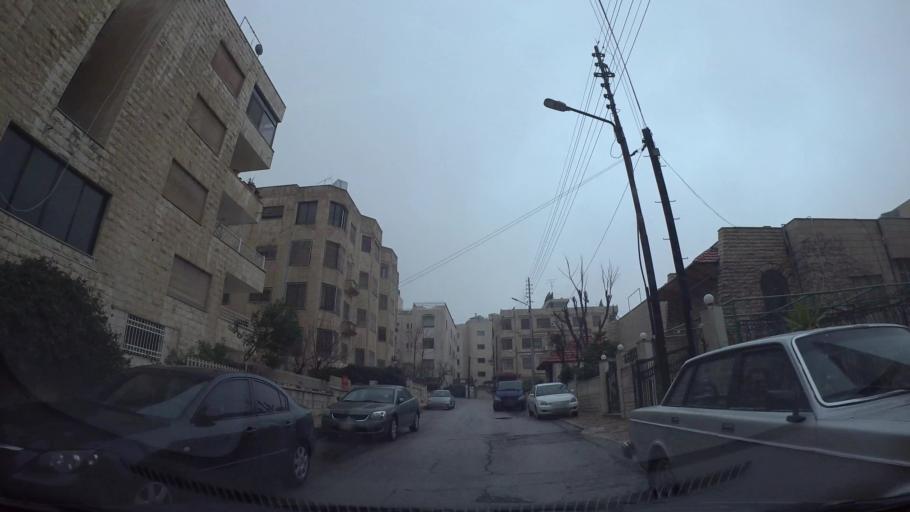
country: JO
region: Amman
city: Al Jubayhah
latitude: 31.9666
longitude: 35.8794
